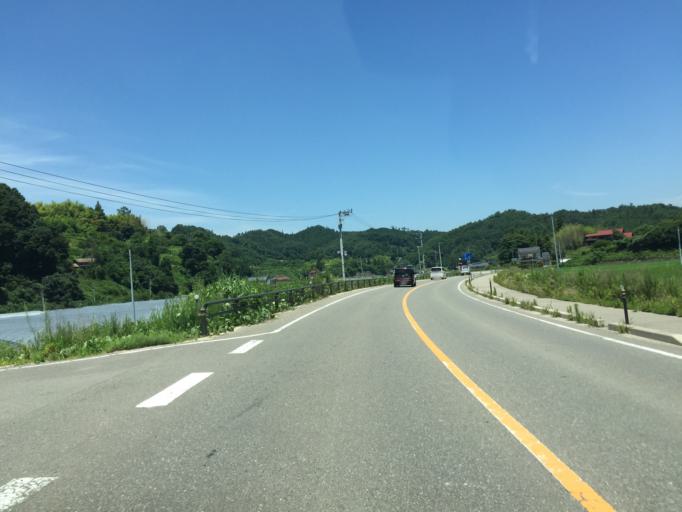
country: JP
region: Fukushima
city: Hobaramachi
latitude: 37.7694
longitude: 140.6106
